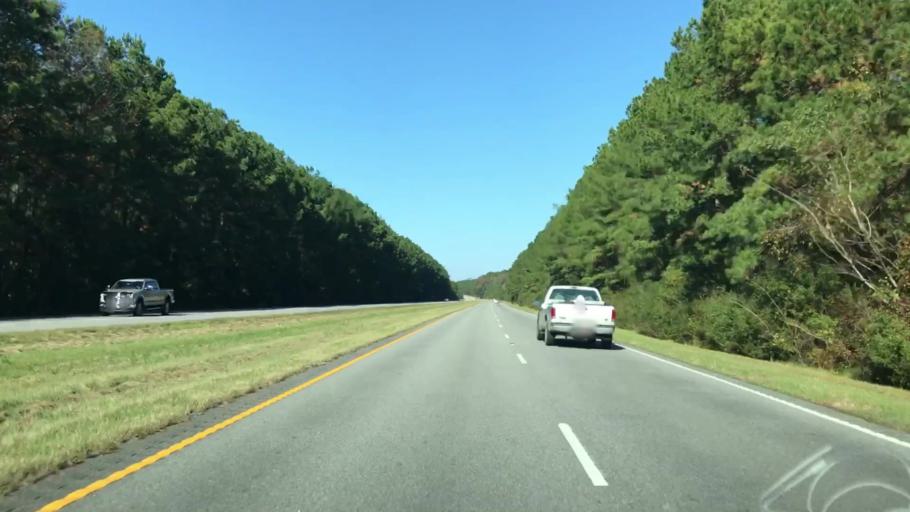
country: US
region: South Carolina
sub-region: Hampton County
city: Yemassee
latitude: 32.6197
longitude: -80.8208
